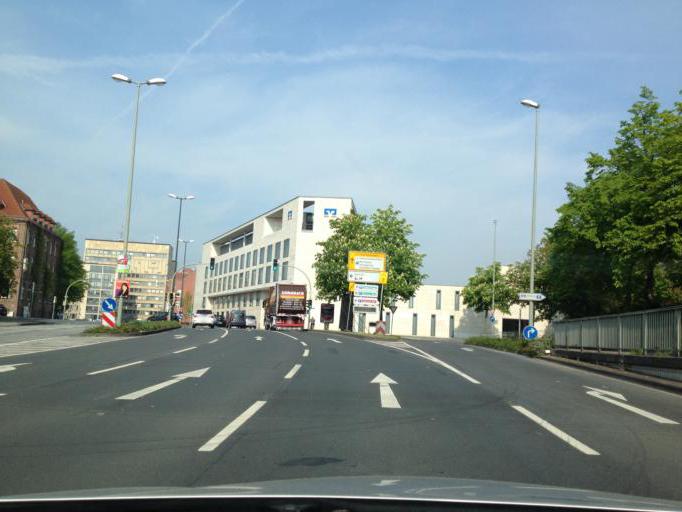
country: DE
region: North Rhine-Westphalia
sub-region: Regierungsbezirk Detmold
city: Guetersloh
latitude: 51.9087
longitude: 8.3859
